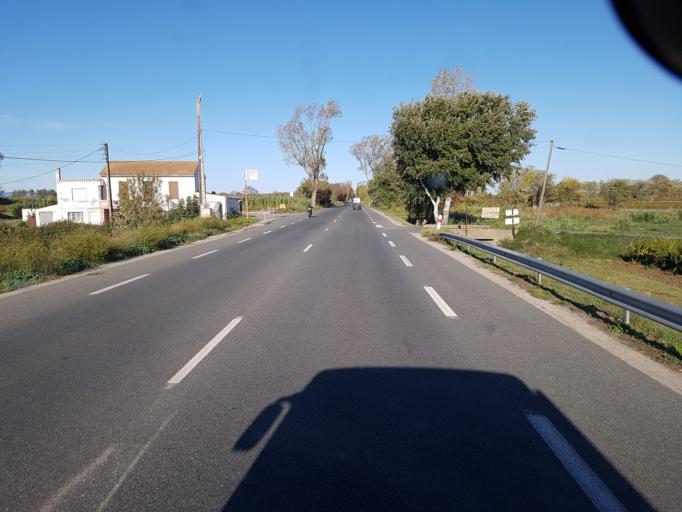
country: FR
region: Languedoc-Roussillon
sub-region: Departement de l'Aude
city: Coursan
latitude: 43.2111
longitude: 3.0293
